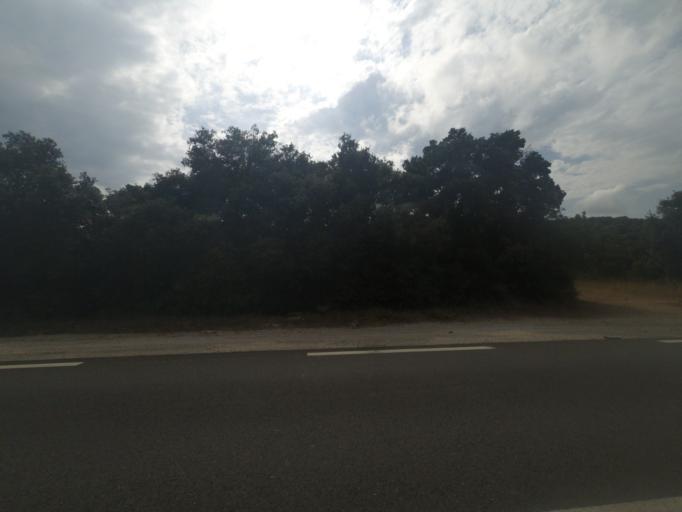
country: FR
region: Languedoc-Roussillon
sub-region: Departement de l'Herault
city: Les Matelles
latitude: 43.7342
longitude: 3.7913
